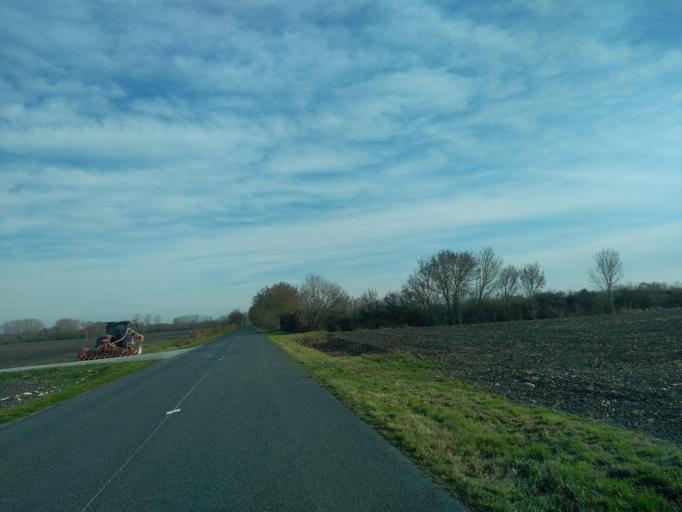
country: FR
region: Pays de la Loire
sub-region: Departement de la Vendee
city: Maillezais
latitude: 46.3786
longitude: -0.7705
